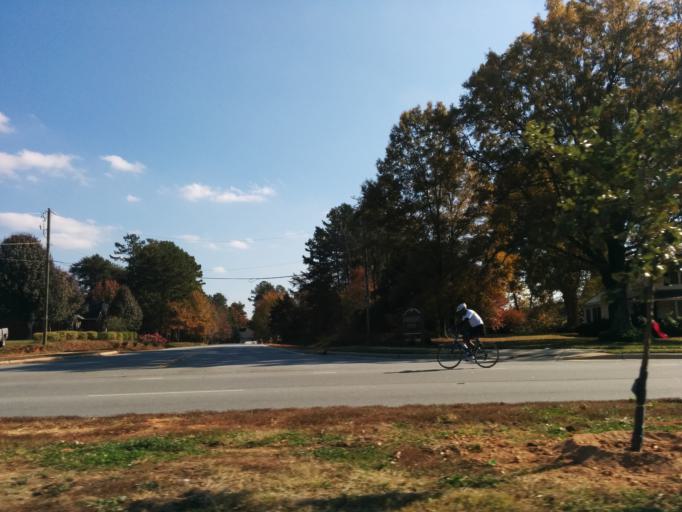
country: US
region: North Carolina
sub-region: Catawba County
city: Lake Norman of Catawba
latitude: 35.5774
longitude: -80.8867
